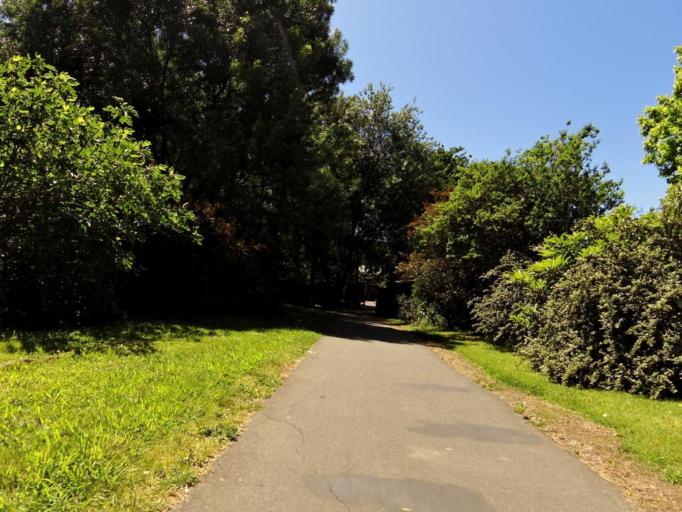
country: AU
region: Victoria
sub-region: Knox
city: Ferntree Gully
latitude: -37.8956
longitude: 145.3085
